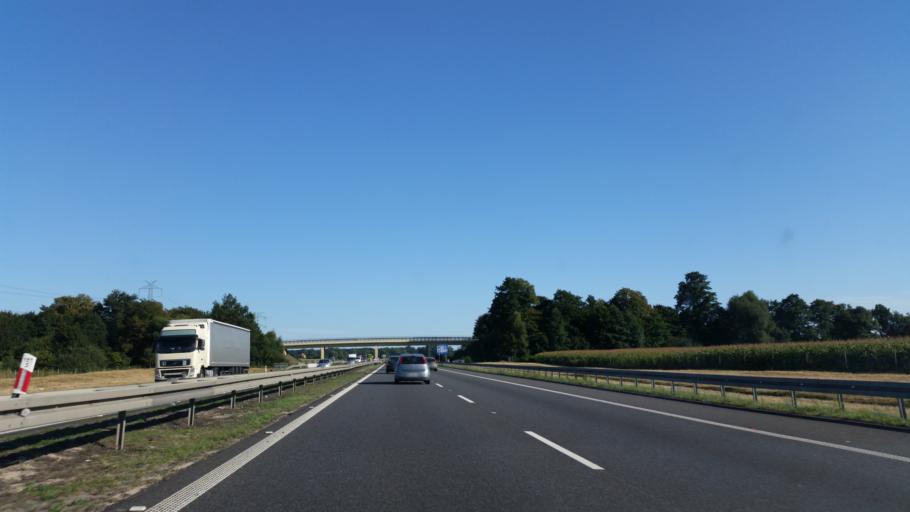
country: PL
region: Lower Silesian Voivodeship
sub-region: Powiat strzelinski
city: Wiazow
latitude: 50.8592
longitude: 17.2247
